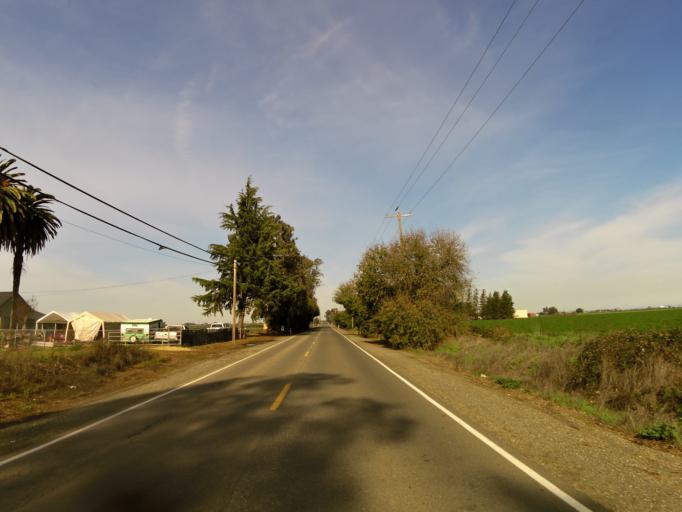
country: US
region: California
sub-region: San Joaquin County
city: Thornton
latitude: 38.3133
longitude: -121.4202
